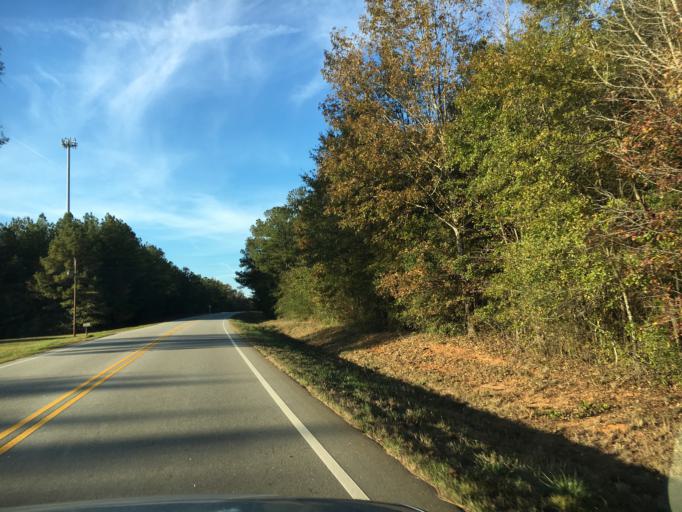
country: US
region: Georgia
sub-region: Elbert County
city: Elberton
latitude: 33.9376
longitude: -82.7664
